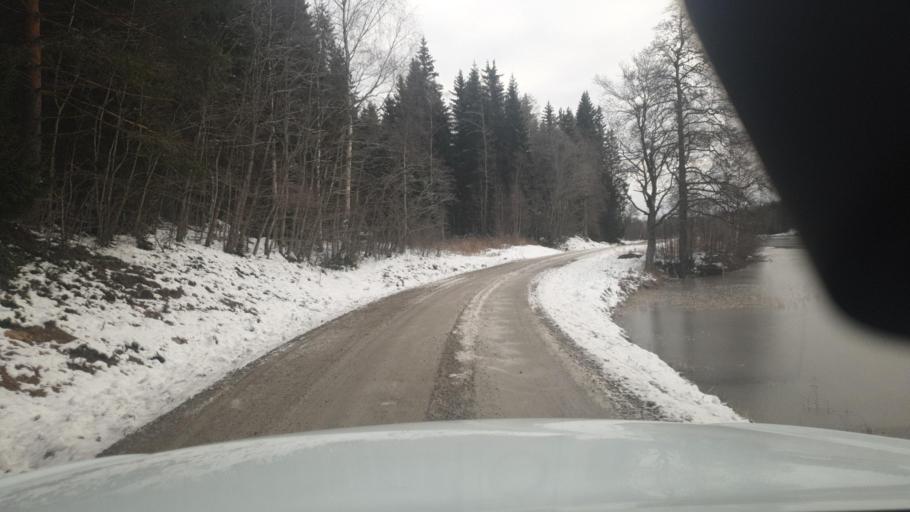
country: SE
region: Vaermland
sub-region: Arvika Kommun
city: Arvika
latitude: 59.8667
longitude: 12.8155
